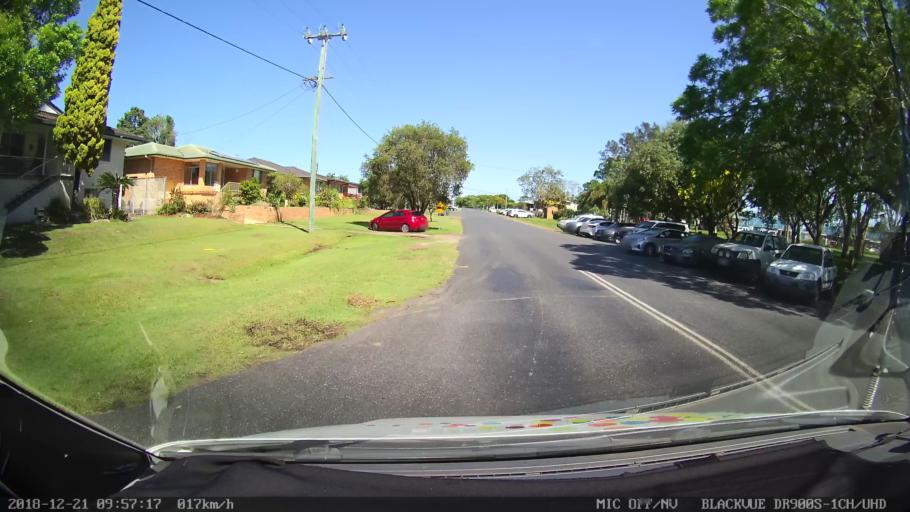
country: AU
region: New South Wales
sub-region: Clarence Valley
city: Grafton
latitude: -29.6752
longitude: 152.9398
